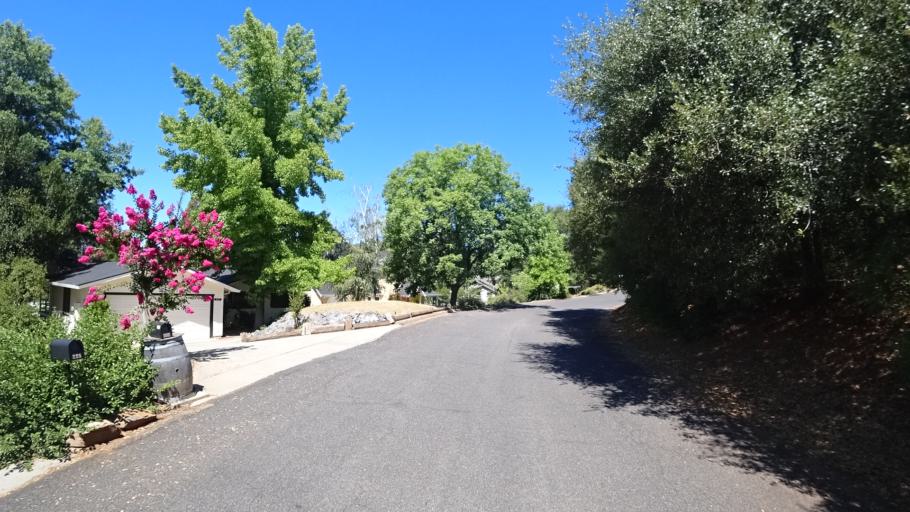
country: US
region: California
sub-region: Calaveras County
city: Murphys
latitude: 38.1450
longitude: -120.4538
